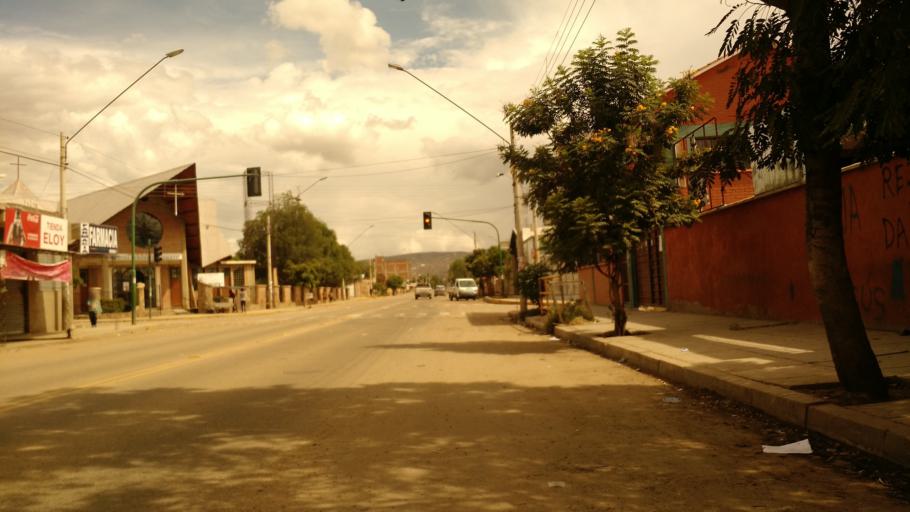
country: BO
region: Cochabamba
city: Cochabamba
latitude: -17.4252
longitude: -66.1233
